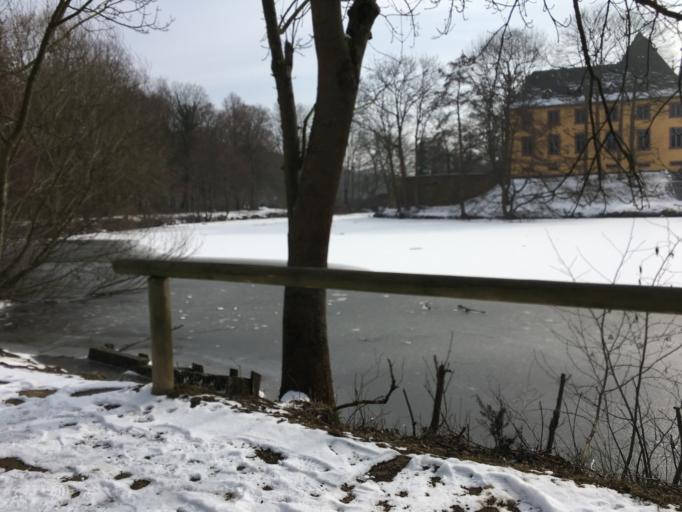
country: DE
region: North Rhine-Westphalia
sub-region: Regierungsbezirk Koln
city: Kreuzau
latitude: 50.7681
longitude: 6.5006
